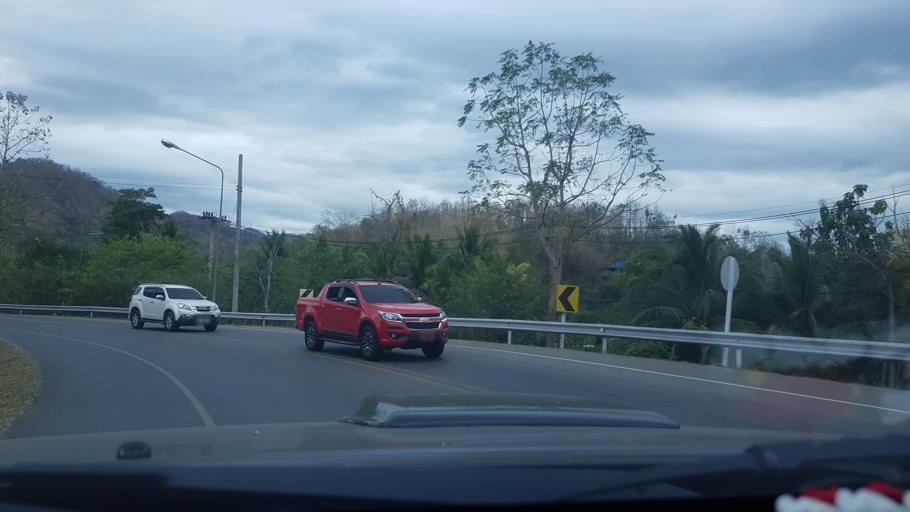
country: TH
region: Phetchabun
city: Phetchabun
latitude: 16.5342
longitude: 101.1003
